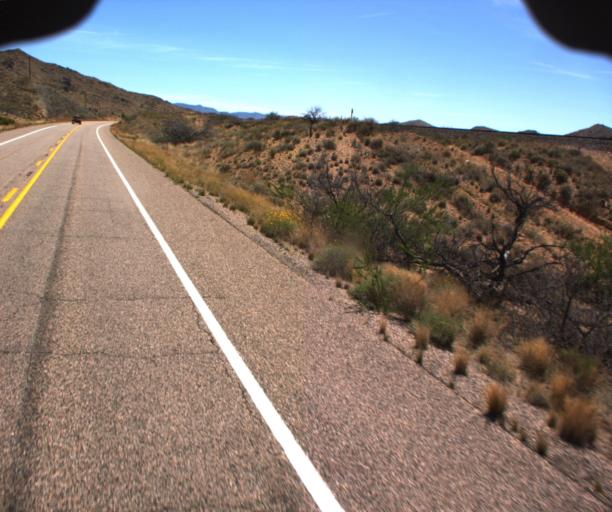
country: US
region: Arizona
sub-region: Mohave County
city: New Kingman-Butler
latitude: 35.3880
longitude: -113.7378
